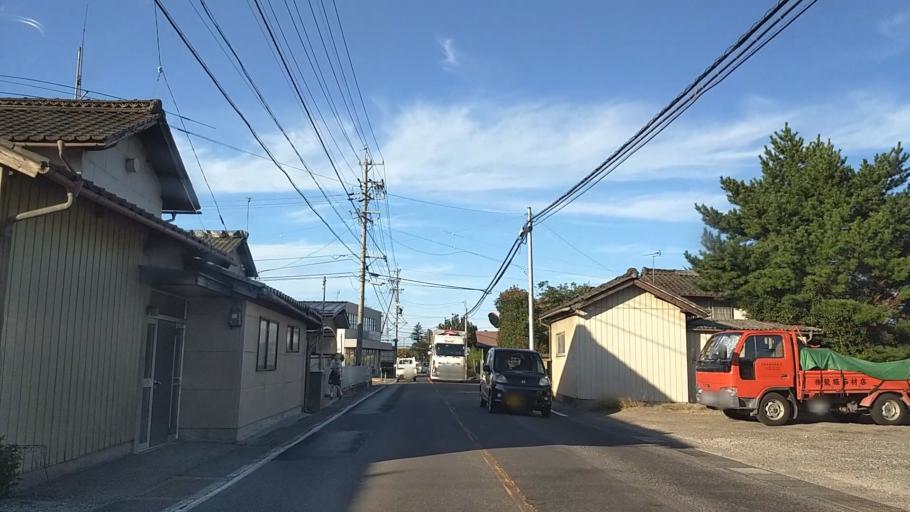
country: JP
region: Nagano
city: Nagano-shi
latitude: 36.5890
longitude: 138.1984
